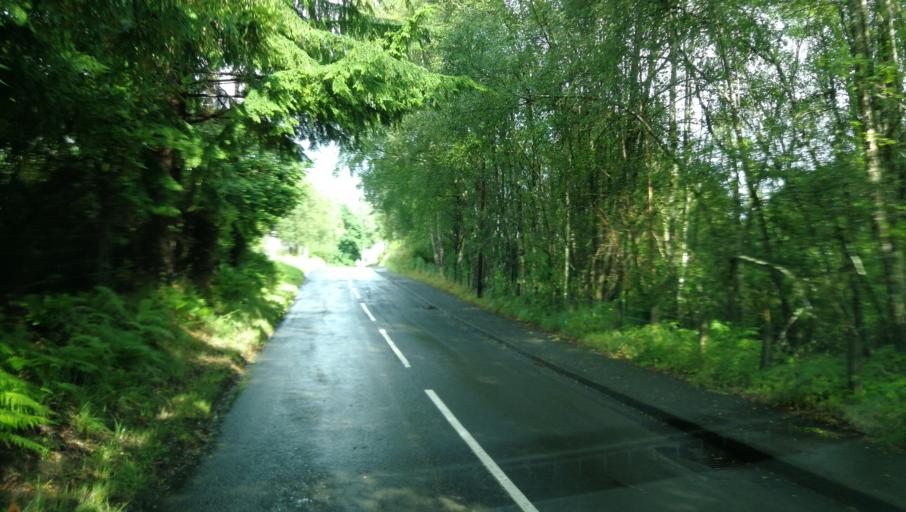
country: GB
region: Scotland
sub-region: Stirling
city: Callander
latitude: 56.2293
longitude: -4.3642
